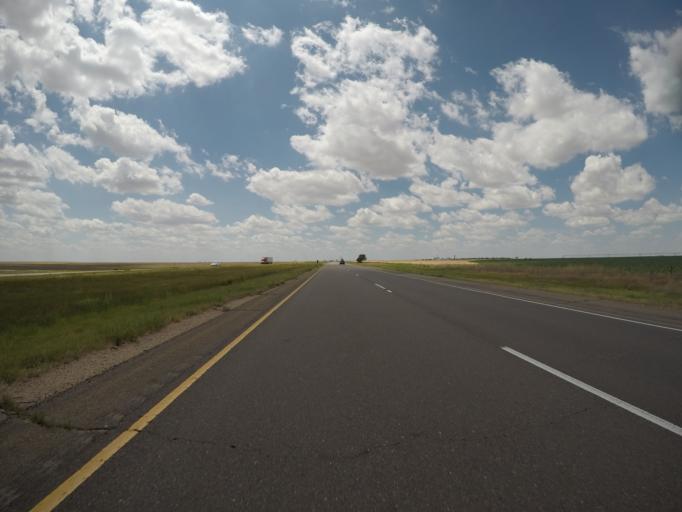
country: US
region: Colorado
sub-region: Kit Carson County
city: Burlington
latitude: 39.2943
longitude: -102.3975
